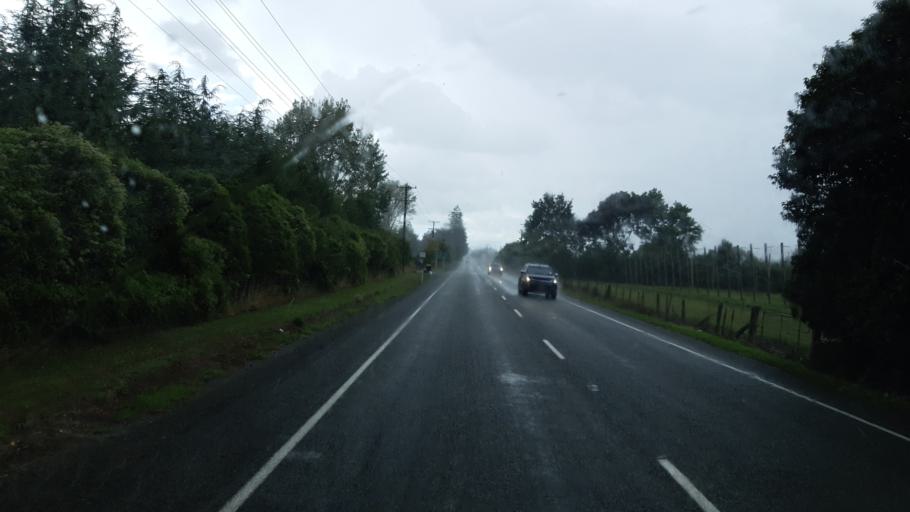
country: NZ
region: Tasman
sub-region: Tasman District
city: Wakefield
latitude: -41.3939
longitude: 173.0672
